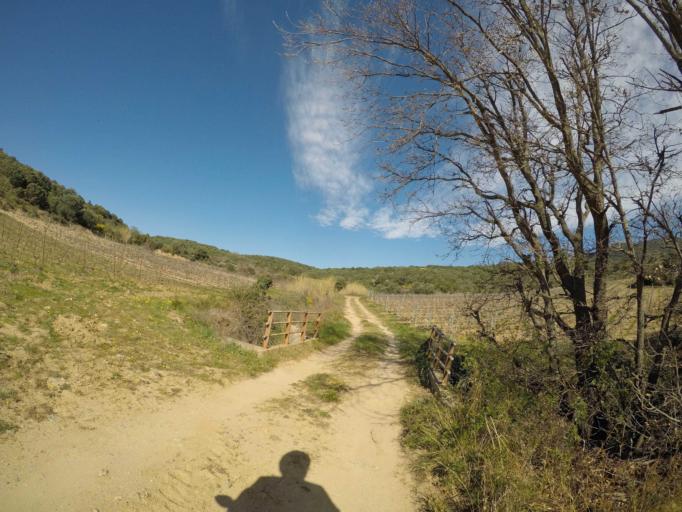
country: FR
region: Languedoc-Roussillon
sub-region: Departement des Pyrenees-Orientales
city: Millas
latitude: 42.7129
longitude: 2.6964
